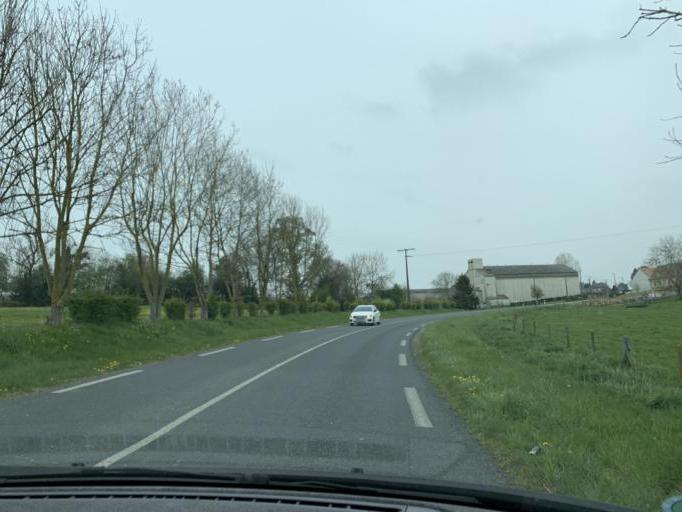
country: FR
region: Haute-Normandie
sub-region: Departement de la Seine-Maritime
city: Londinieres
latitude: 49.8436
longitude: 1.4704
